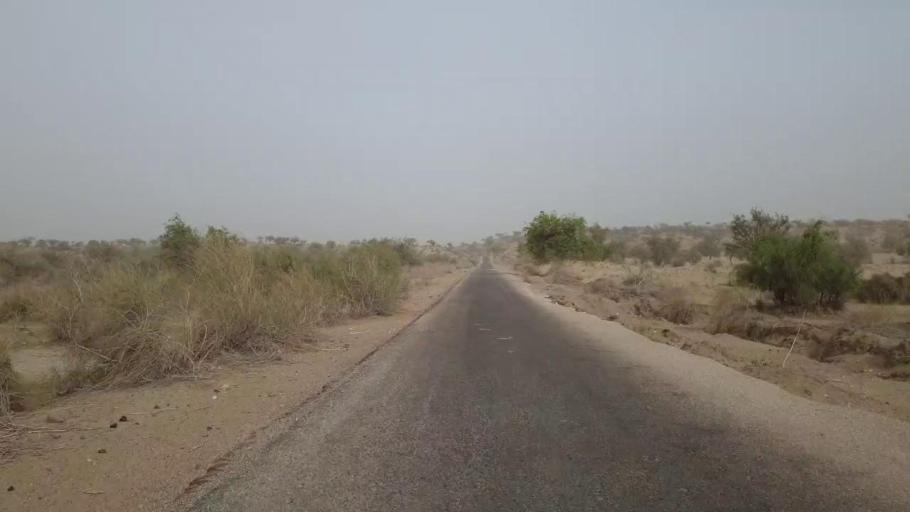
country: PK
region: Sindh
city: Islamkot
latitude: 24.5899
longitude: 70.2891
